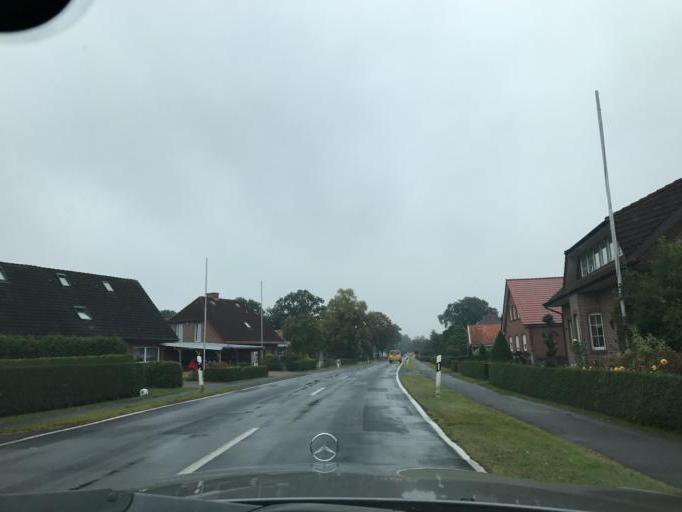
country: DE
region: Lower Saxony
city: Papenburg
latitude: 53.0677
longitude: 7.3437
